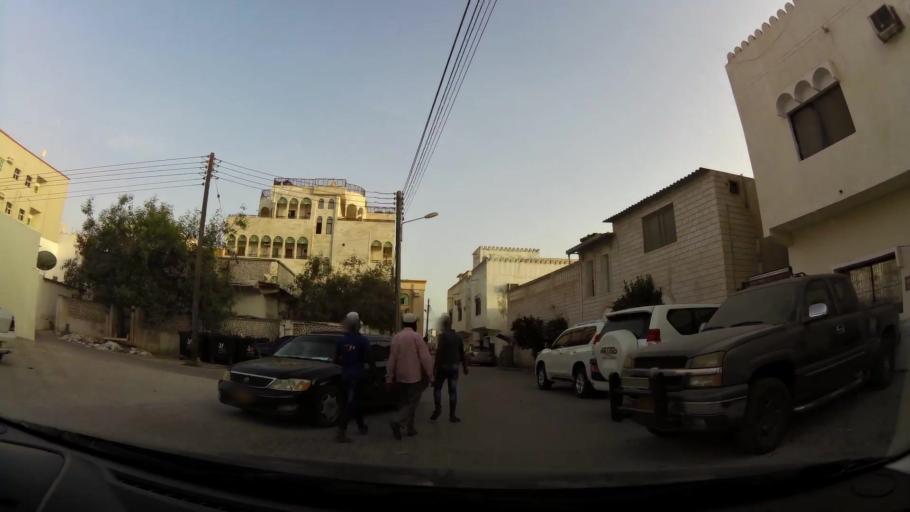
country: OM
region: Zufar
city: Salalah
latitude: 17.0160
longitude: 54.1102
